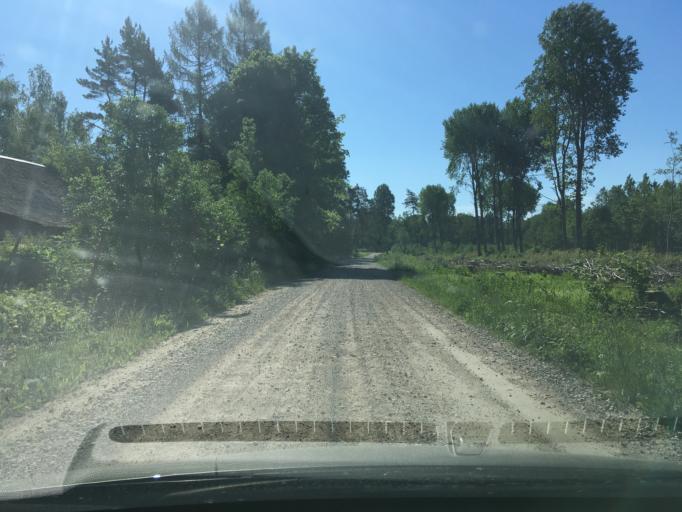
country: EE
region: Laeaene
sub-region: Lihula vald
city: Lihula
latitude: 58.6462
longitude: 23.7824
